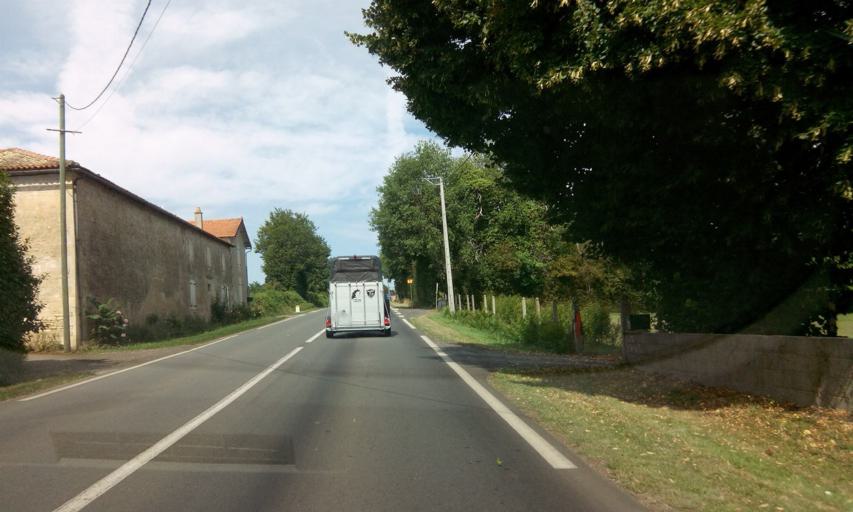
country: FR
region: Poitou-Charentes
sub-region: Departement des Deux-Sevres
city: Sauze-Vaussais
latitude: 46.1524
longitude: 0.0577
